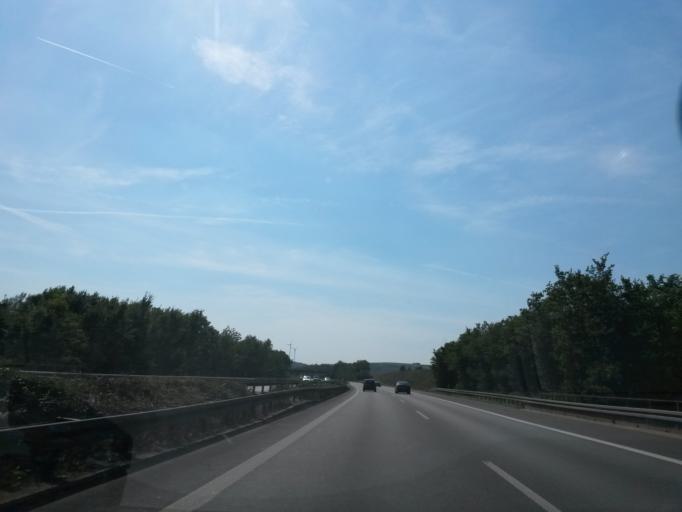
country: DE
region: Bavaria
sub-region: Regierungsbezirk Unterfranken
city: Dettelbach
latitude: 49.7891
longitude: 10.1759
